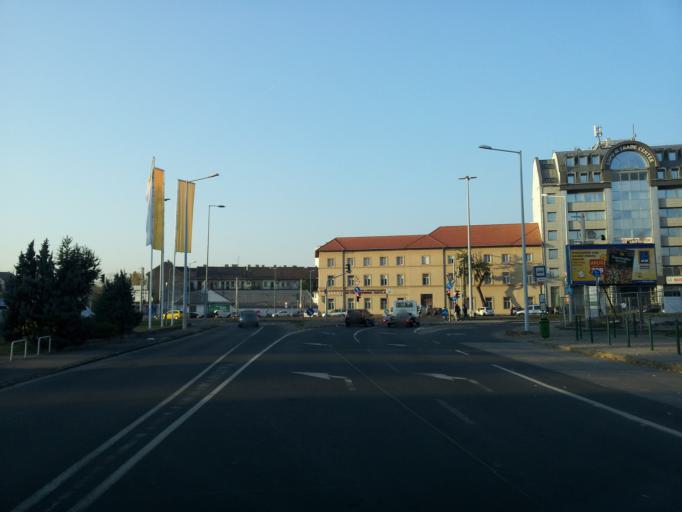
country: HU
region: Budapest
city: Budapest XIV. keruelet
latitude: 47.5002
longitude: 19.1156
